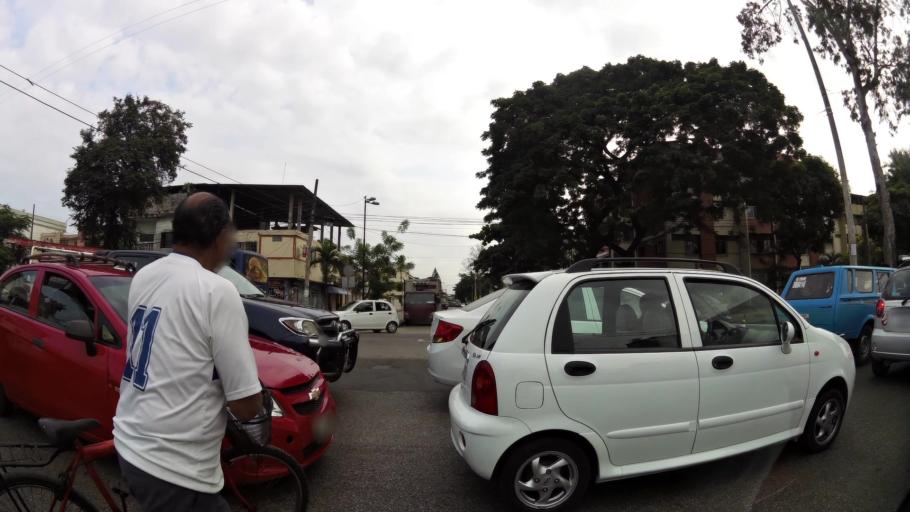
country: EC
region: Guayas
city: Guayaquil
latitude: -2.2391
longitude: -79.8931
